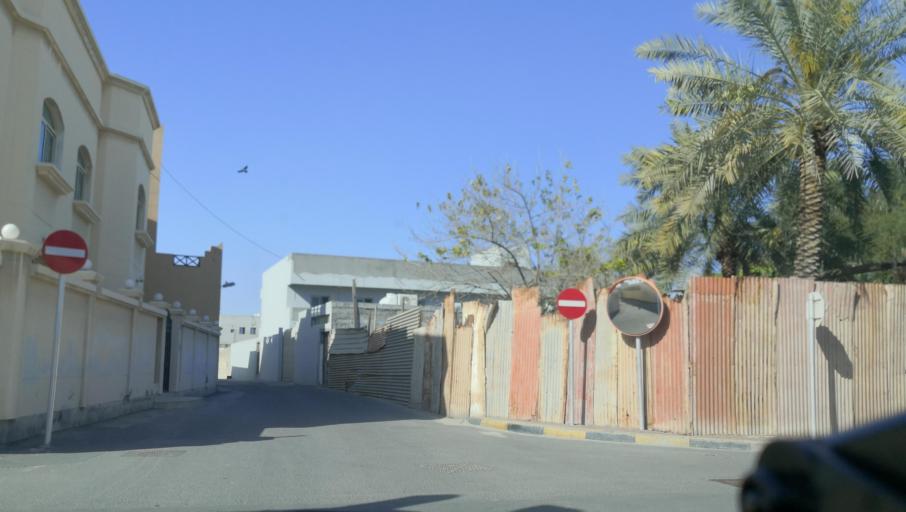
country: BH
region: Muharraq
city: Al Hadd
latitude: 26.2542
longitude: 50.6339
